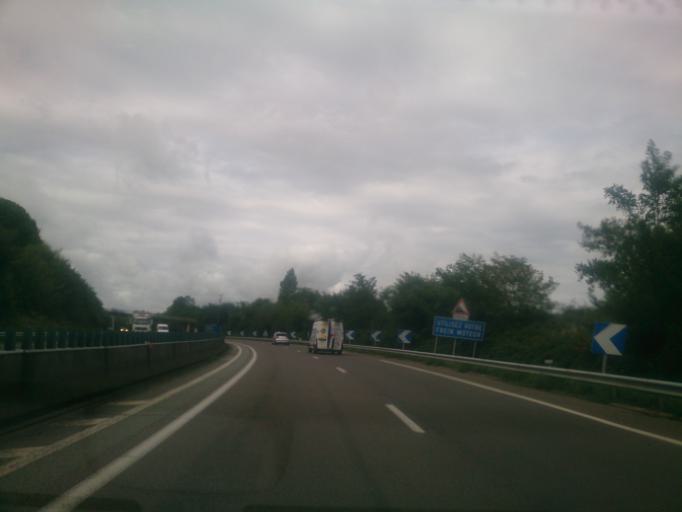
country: FR
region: Midi-Pyrenees
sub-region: Departement des Hautes-Pyrenees
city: Capvern
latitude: 43.1070
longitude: 0.3315
